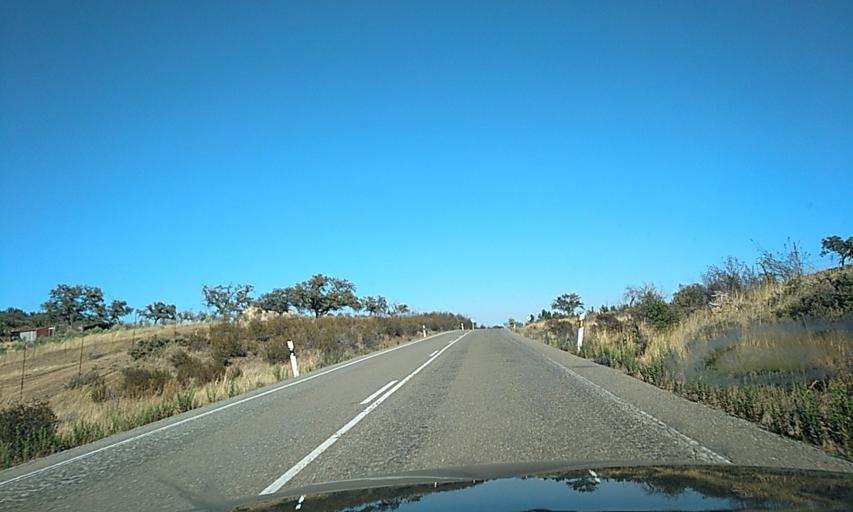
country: ES
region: Andalusia
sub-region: Provincia de Huelva
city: Santa Barbara de Casa
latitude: 37.7889
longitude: -7.1712
